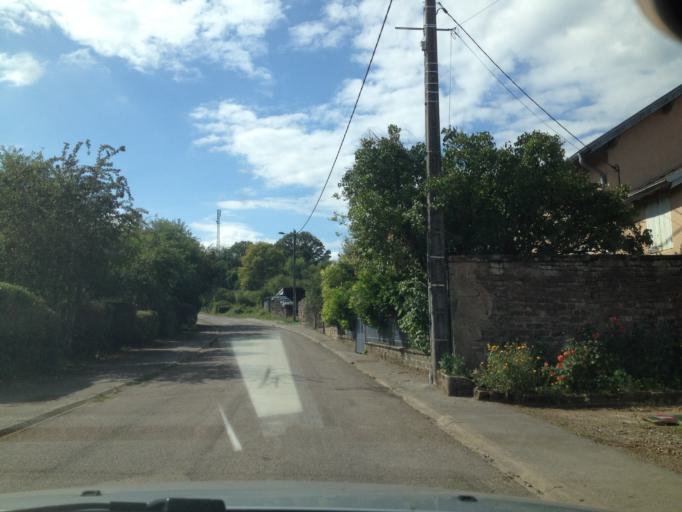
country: FR
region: Lorraine
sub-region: Departement des Vosges
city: Bains-les-Bains
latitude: 47.9332
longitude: 6.1610
